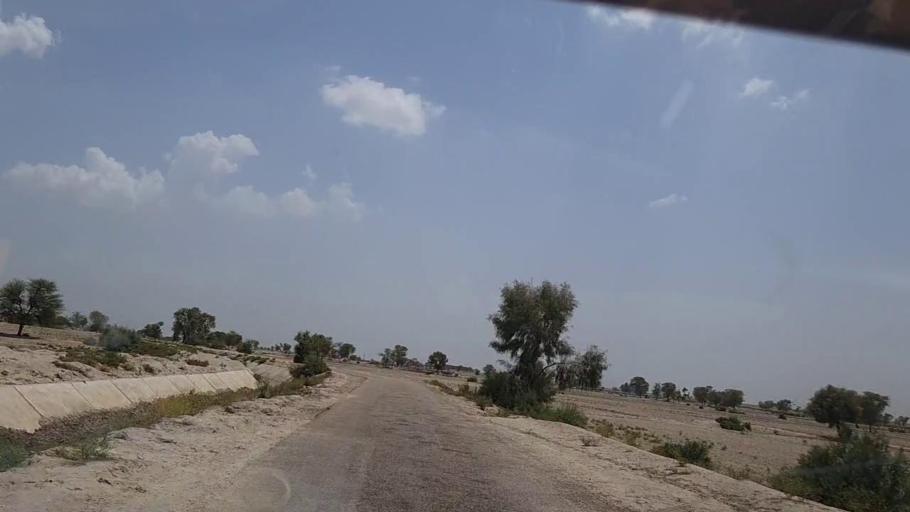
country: PK
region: Sindh
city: Bhan
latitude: 26.5335
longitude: 67.6324
